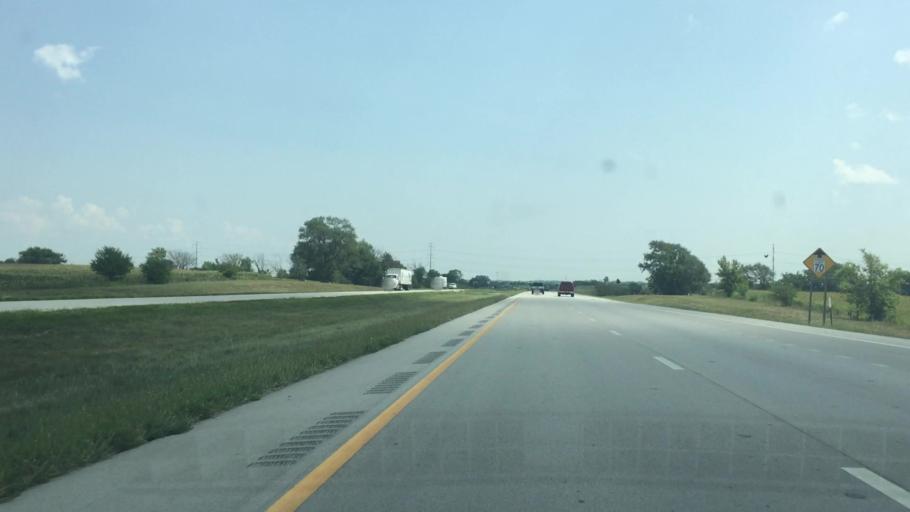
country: US
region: Kansas
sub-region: Johnson County
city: Edgerton
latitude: 38.7476
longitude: -94.9955
